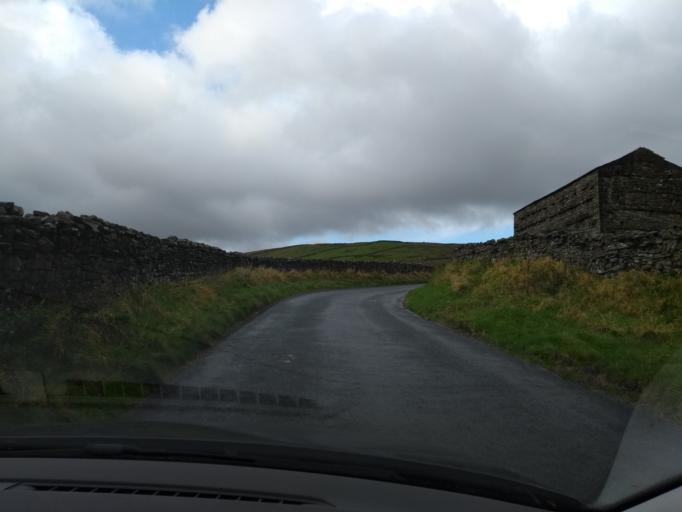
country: GB
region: England
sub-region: Cumbria
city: Kirkby Stephen
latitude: 54.3801
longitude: -2.1707
